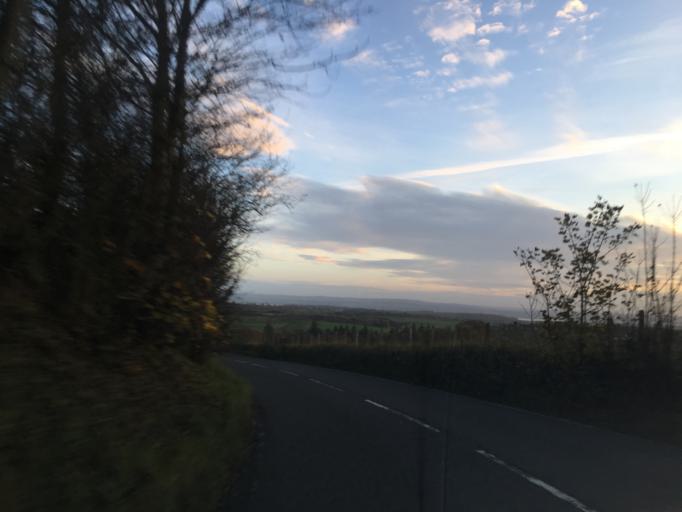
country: GB
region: Scotland
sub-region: Fife
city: Saline
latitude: 56.1108
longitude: -3.5645
